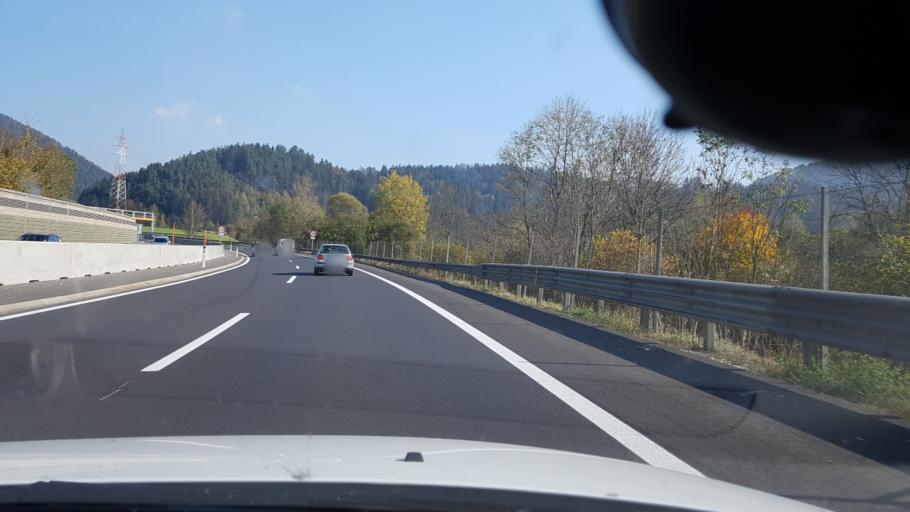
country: AT
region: Styria
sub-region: Politischer Bezirk Leoben
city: Sankt Michael in Obersteiermark
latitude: 47.3334
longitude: 15.0270
